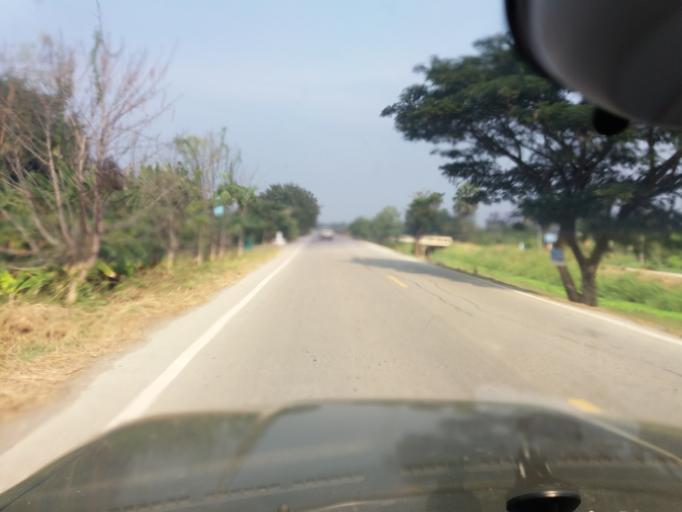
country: TH
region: Sing Buri
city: Bang Racham
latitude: 14.8948
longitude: 100.2704
